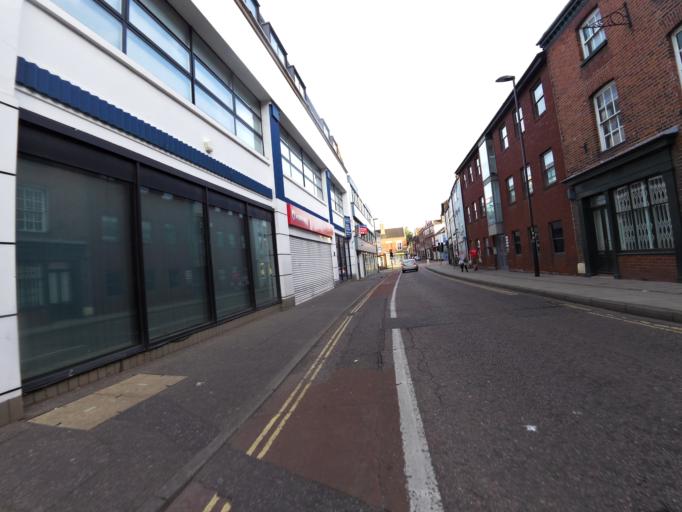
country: GB
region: England
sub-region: Norfolk
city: Norwich
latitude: 52.6288
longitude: 1.2993
